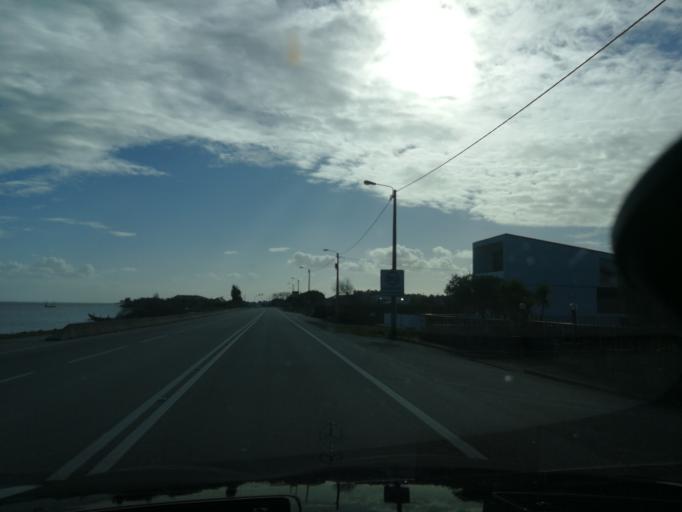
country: PT
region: Aveiro
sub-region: Murtosa
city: Murtosa
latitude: 40.7729
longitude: -8.6939
